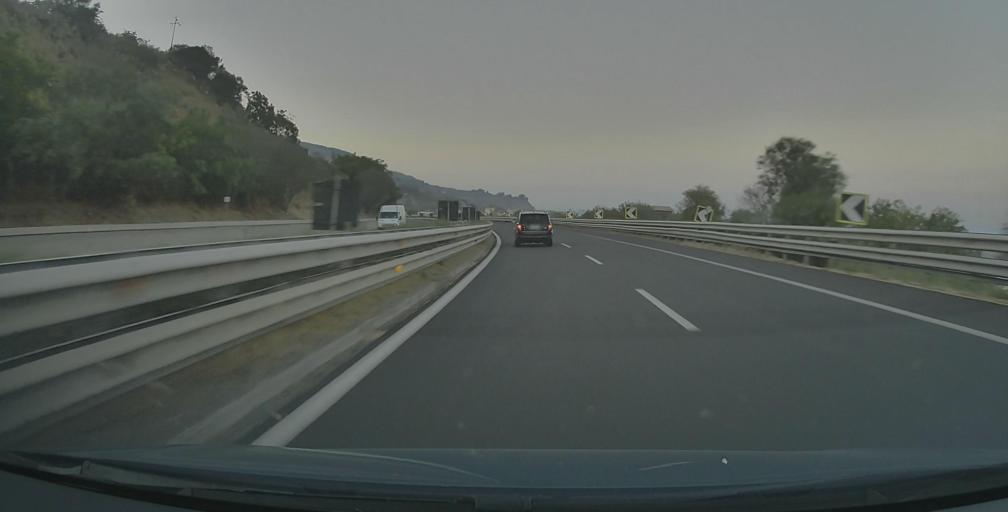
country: IT
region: Sicily
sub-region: Messina
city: Nizza di Sicilia
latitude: 37.9918
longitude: 15.4094
